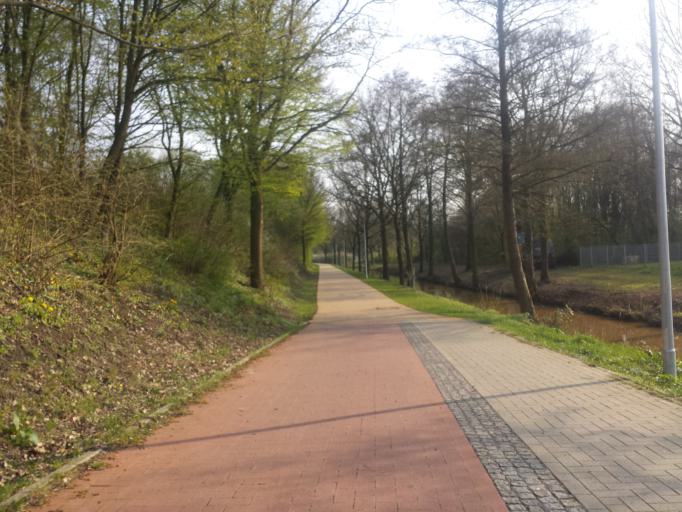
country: DE
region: Lower Saxony
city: Lilienthal
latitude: 53.0689
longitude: 8.9023
